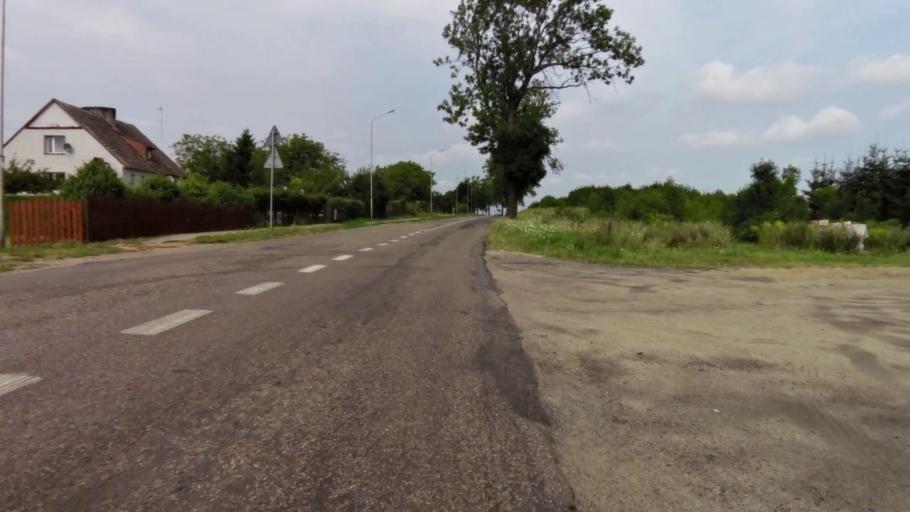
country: PL
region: West Pomeranian Voivodeship
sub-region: Powiat drawski
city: Drawsko Pomorskie
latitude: 53.5524
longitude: 15.8234
